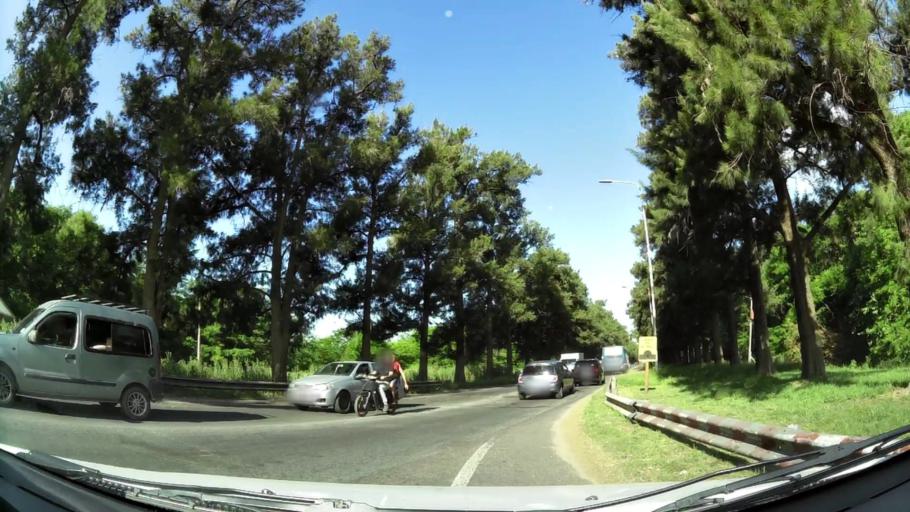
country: AR
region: Buenos Aires
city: Hurlingham
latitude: -34.5630
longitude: -58.6411
